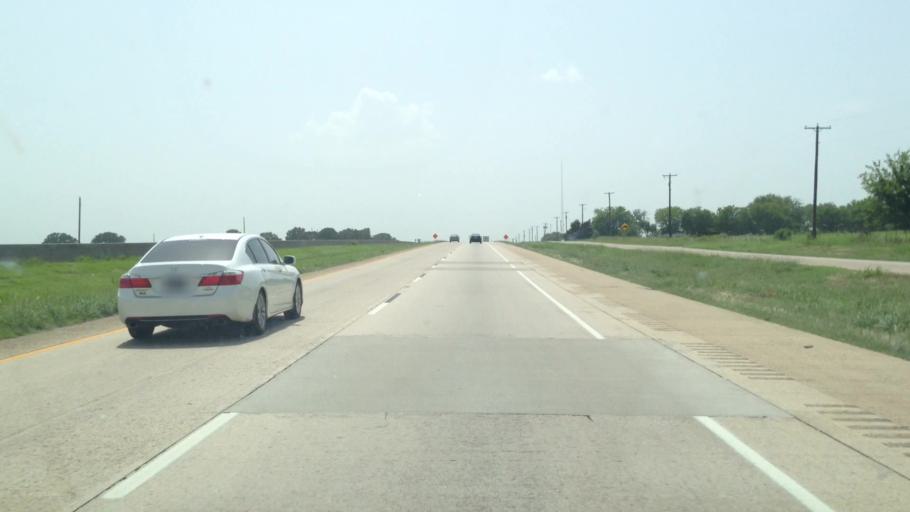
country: US
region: Texas
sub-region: Hopkins County
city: Sulphur Springs
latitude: 33.1209
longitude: -95.6968
